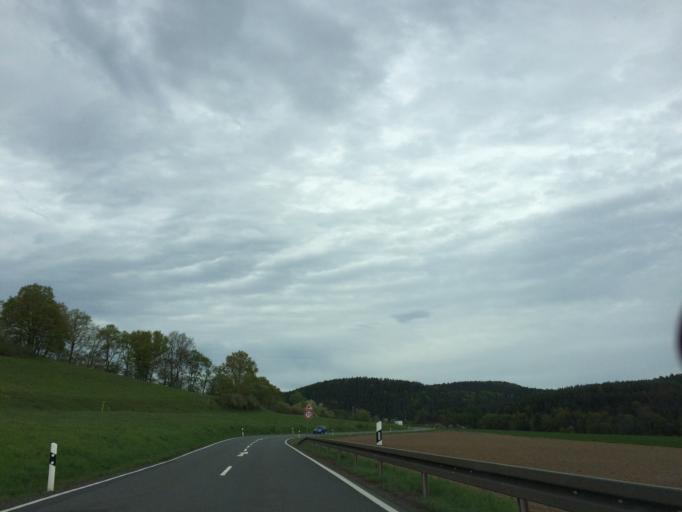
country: DE
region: Thuringia
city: Langenorla
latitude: 50.7241
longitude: 11.6016
